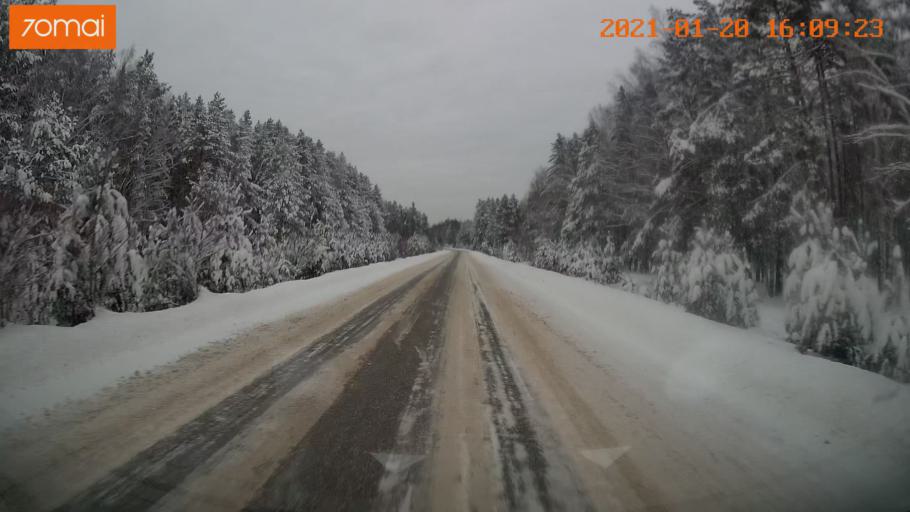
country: RU
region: Vladimir
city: Sudogda
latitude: 56.0813
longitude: 40.7771
